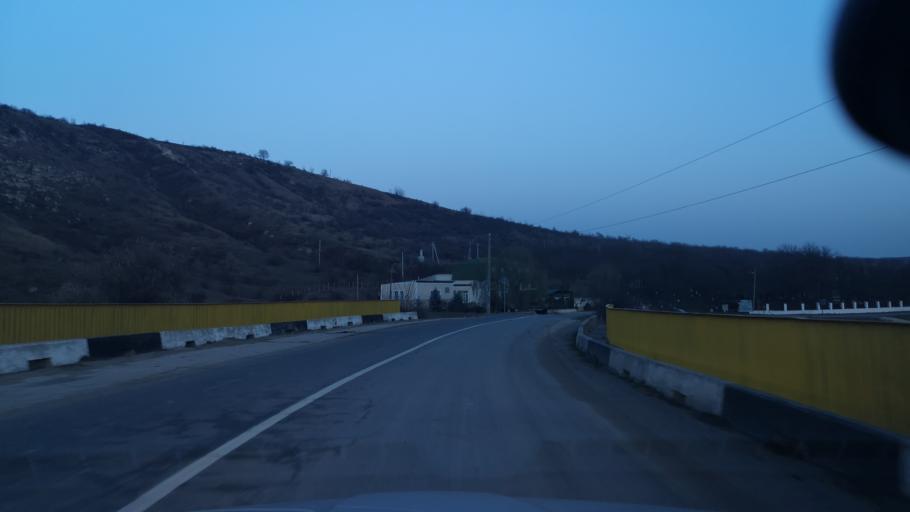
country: MD
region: Telenesti
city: Cocieri
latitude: 47.3075
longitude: 28.9624
